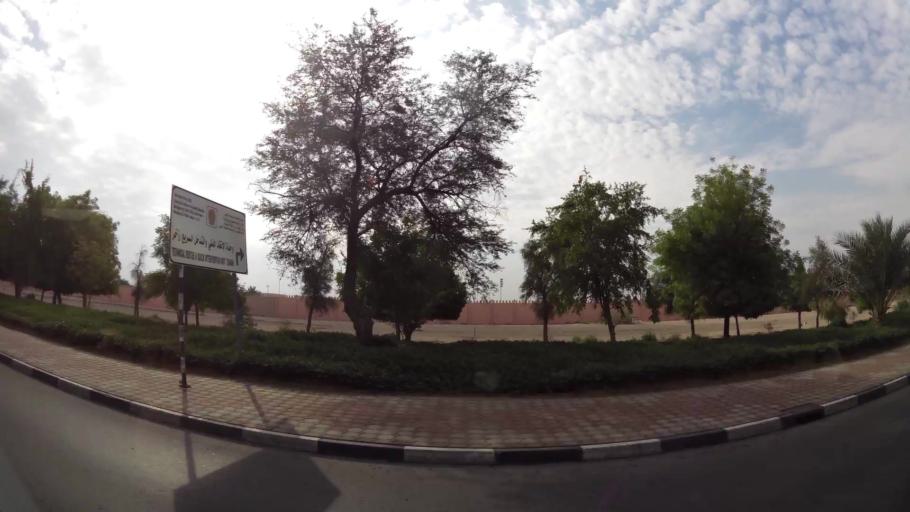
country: AE
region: Abu Dhabi
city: Al Ain
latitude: 24.1916
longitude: 55.6482
